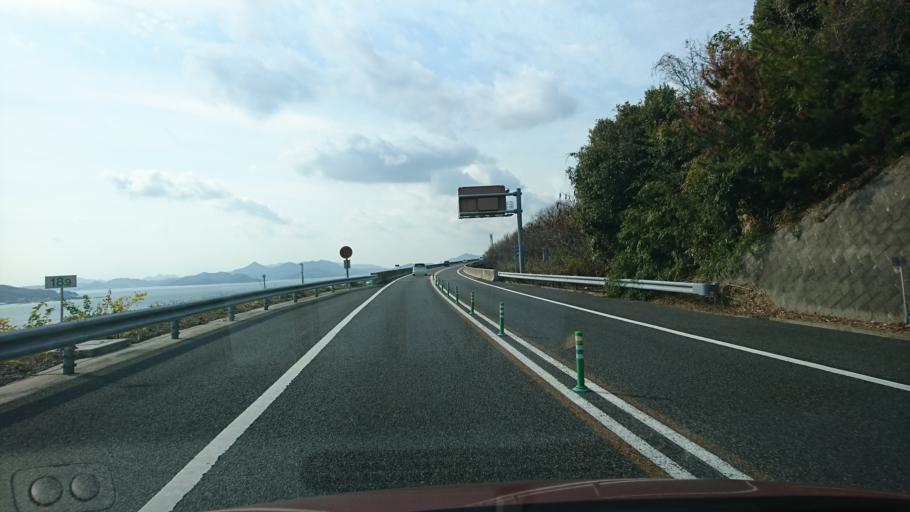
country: JP
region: Hiroshima
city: Innoshima
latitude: 34.2915
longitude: 133.1421
